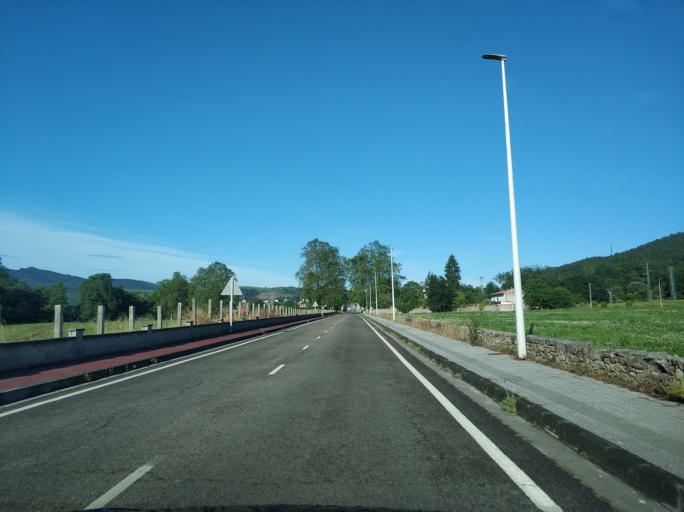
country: ES
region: Cantabria
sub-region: Provincia de Cantabria
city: Polanco
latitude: 43.3522
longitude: -3.9783
